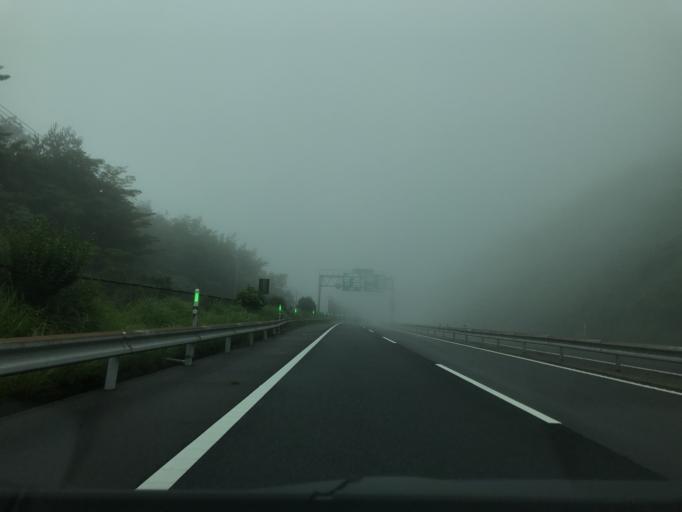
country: JP
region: Oita
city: Hiji
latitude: 33.3616
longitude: 131.4511
